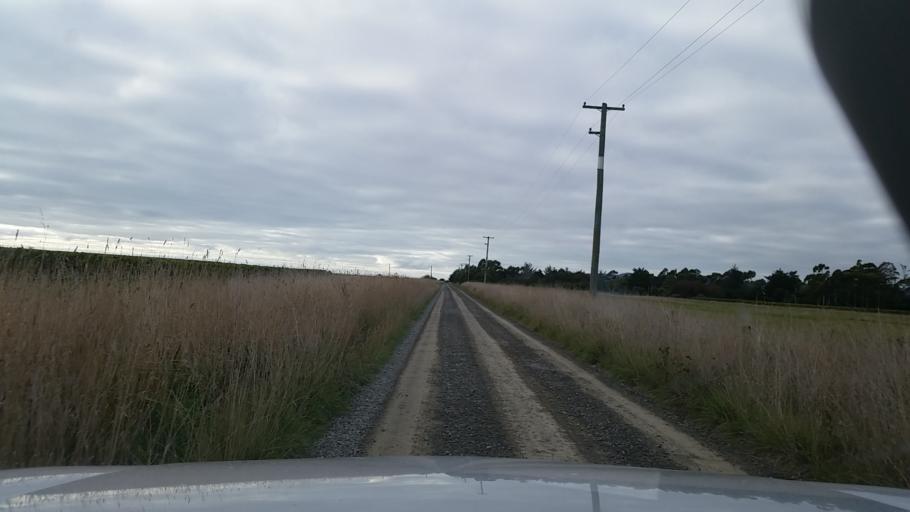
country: NZ
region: Marlborough
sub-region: Marlborough District
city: Blenheim
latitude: -41.5109
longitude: 174.0366
